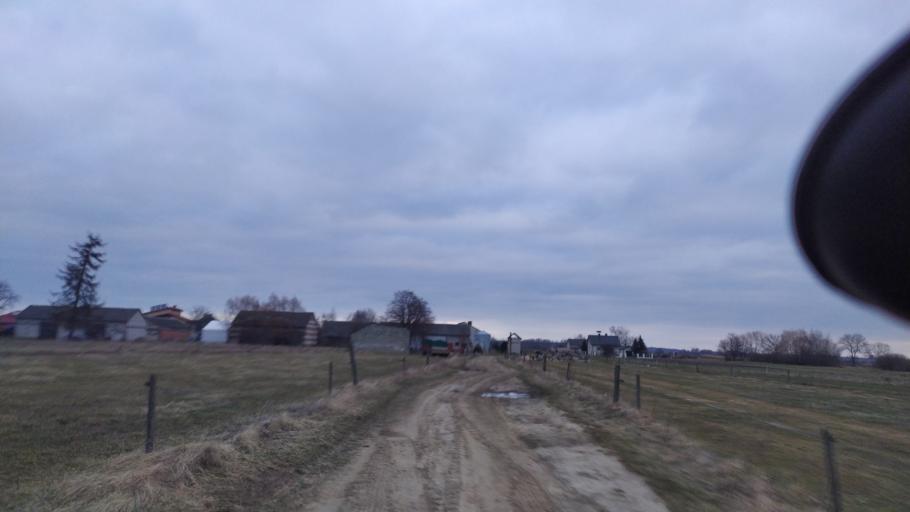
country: PL
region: Lublin Voivodeship
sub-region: Powiat lubartowski
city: Abramow
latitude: 51.4385
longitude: 22.2959
